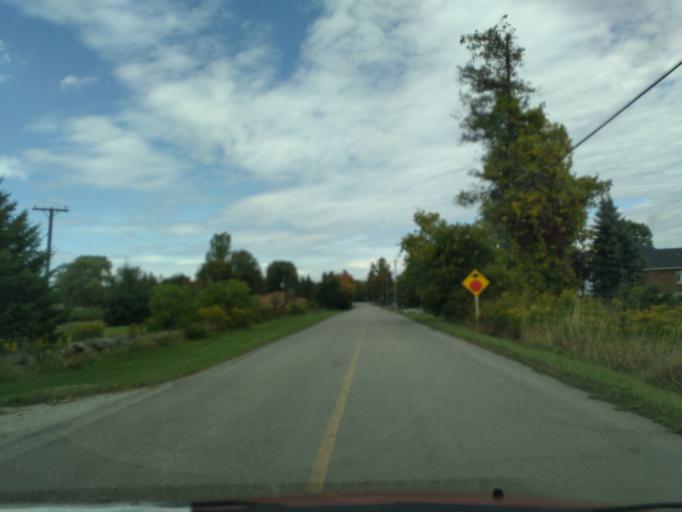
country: CA
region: Ontario
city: Keswick
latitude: 44.2696
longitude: -79.3663
